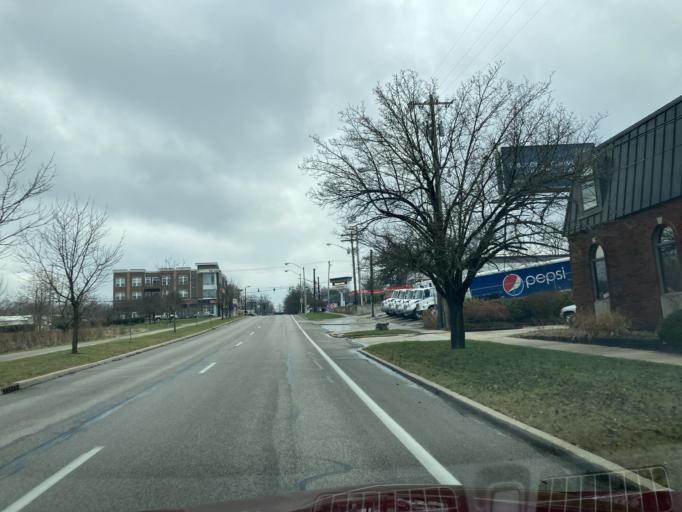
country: US
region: Indiana
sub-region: Monroe County
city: Bloomington
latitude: 39.1802
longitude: -86.5347
